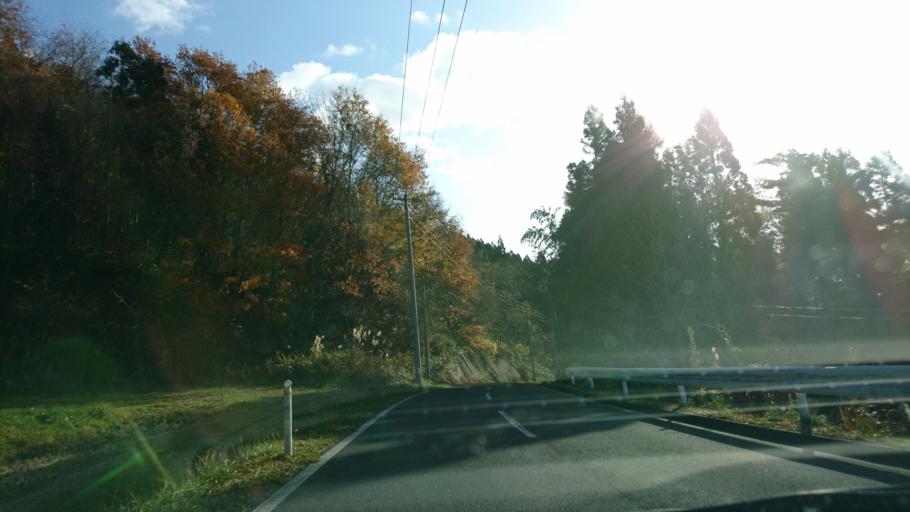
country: JP
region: Iwate
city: Ichinoseki
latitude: 38.8719
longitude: 141.3051
